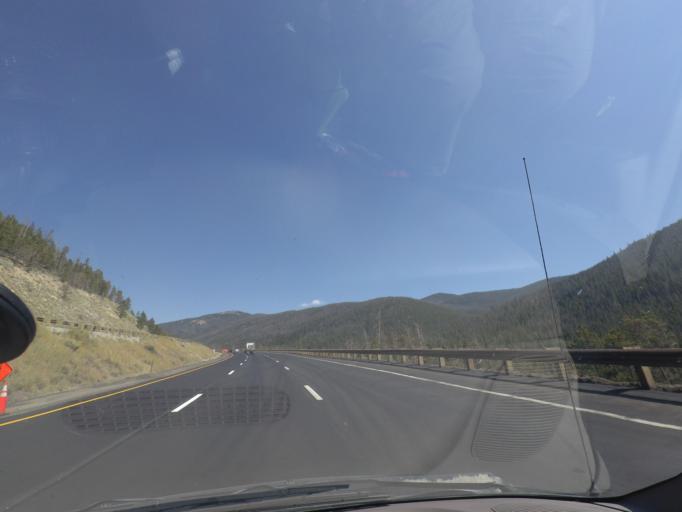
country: US
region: Colorado
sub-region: Summit County
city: Keystone
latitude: 39.6525
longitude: -106.0041
